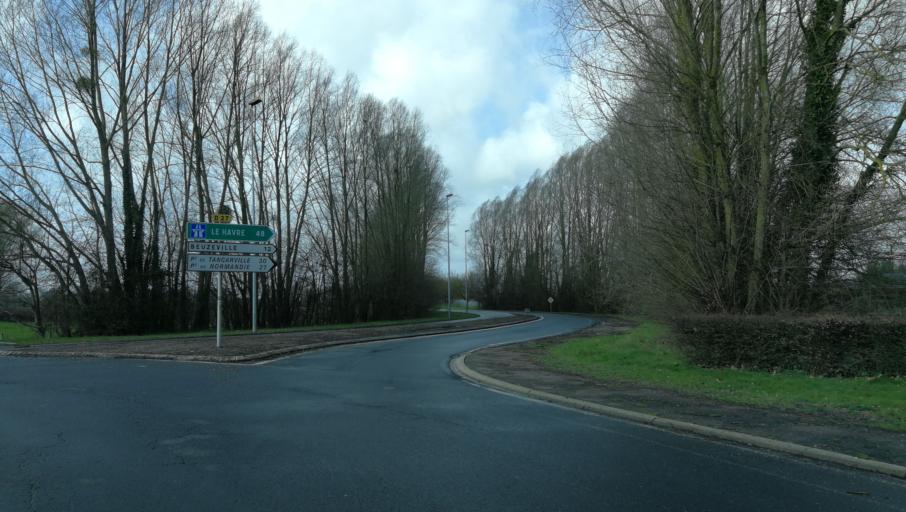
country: FR
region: Haute-Normandie
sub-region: Departement de l'Eure
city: Epaignes
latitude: 49.2778
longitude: 0.4354
